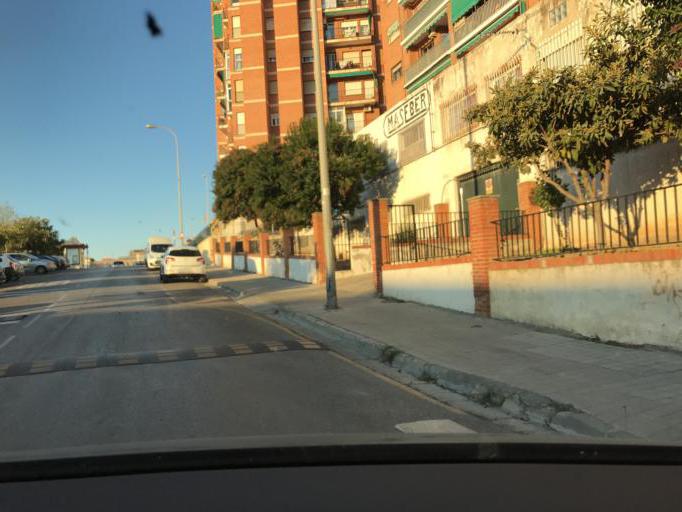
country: ES
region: Andalusia
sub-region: Provincia de Granada
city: Granada
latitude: 37.1968
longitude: -3.6024
